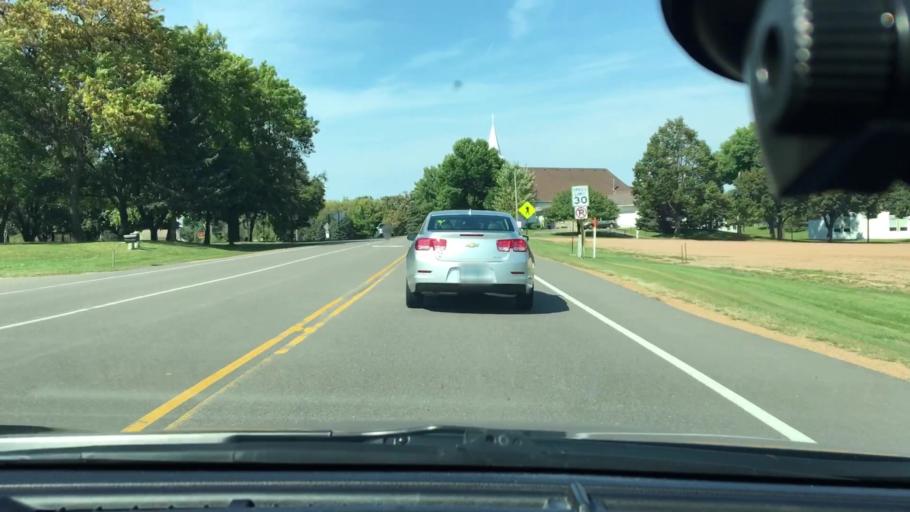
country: US
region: Minnesota
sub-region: Hennepin County
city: Corcoran
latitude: 45.0939
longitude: -93.5435
